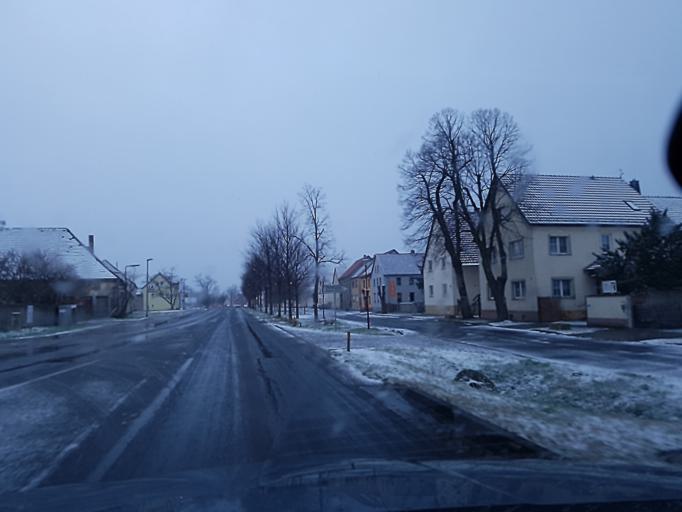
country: DE
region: Brandenburg
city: Elsterwerda
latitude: 51.4543
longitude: 13.5281
